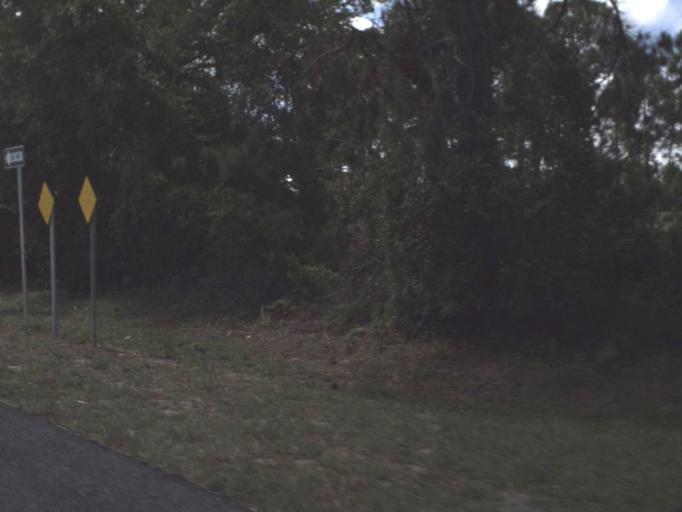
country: US
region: Florida
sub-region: Flagler County
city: Bunnell
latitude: 29.3917
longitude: -81.1911
